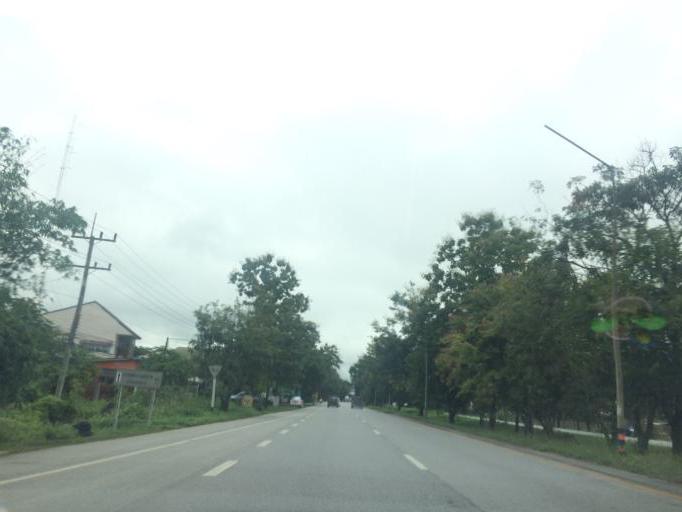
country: TH
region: Chiang Rai
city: Mae Lao
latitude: 19.7704
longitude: 99.7374
